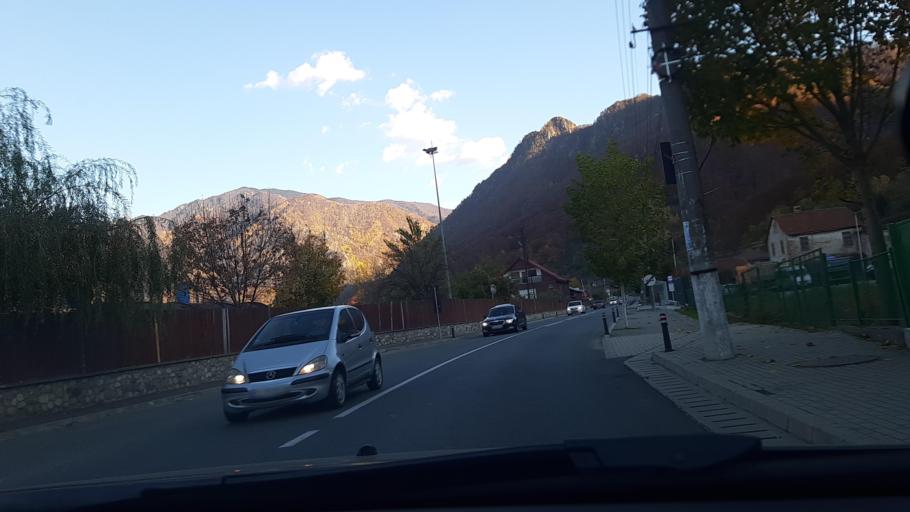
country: RO
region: Valcea
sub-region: Comuna Brezoi
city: Brezoi
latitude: 45.3361
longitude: 24.2512
